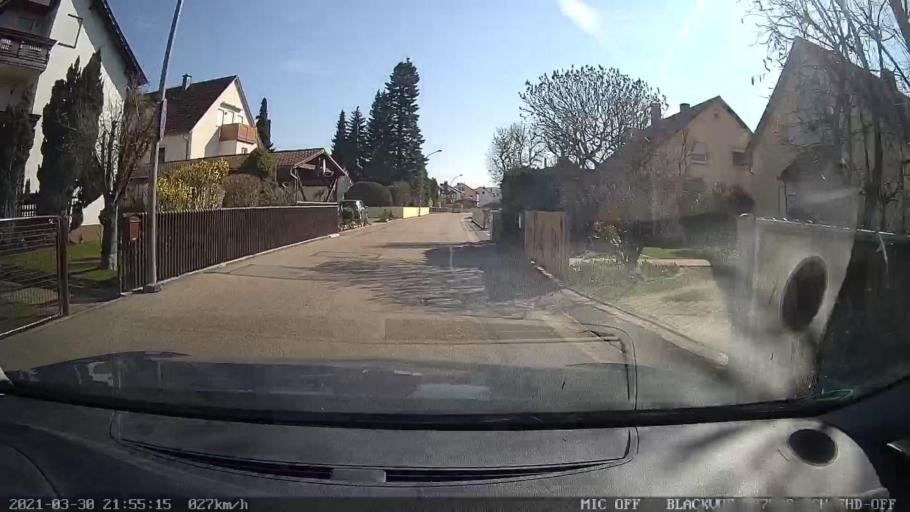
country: DE
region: Bavaria
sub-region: Upper Palatinate
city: Zeitlarn
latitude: 49.0985
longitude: 12.1122
